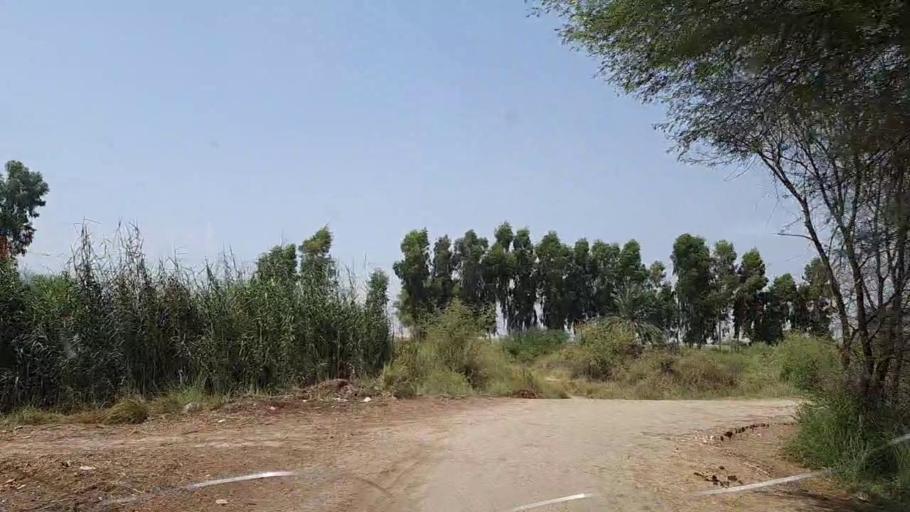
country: PK
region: Sindh
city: Ghotki
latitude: 28.0717
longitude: 69.3174
